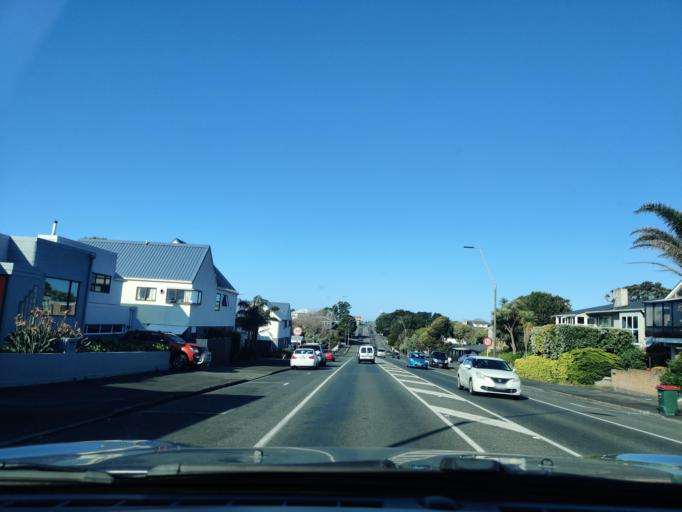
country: NZ
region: Taranaki
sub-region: New Plymouth District
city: New Plymouth
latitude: -39.0530
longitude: 174.0899
